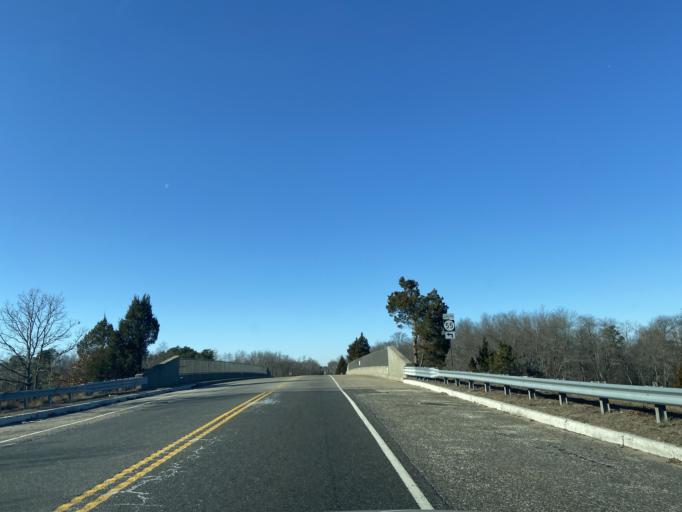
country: US
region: New Jersey
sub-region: Gloucester County
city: Newfield
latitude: 39.5219
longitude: -75.0680
